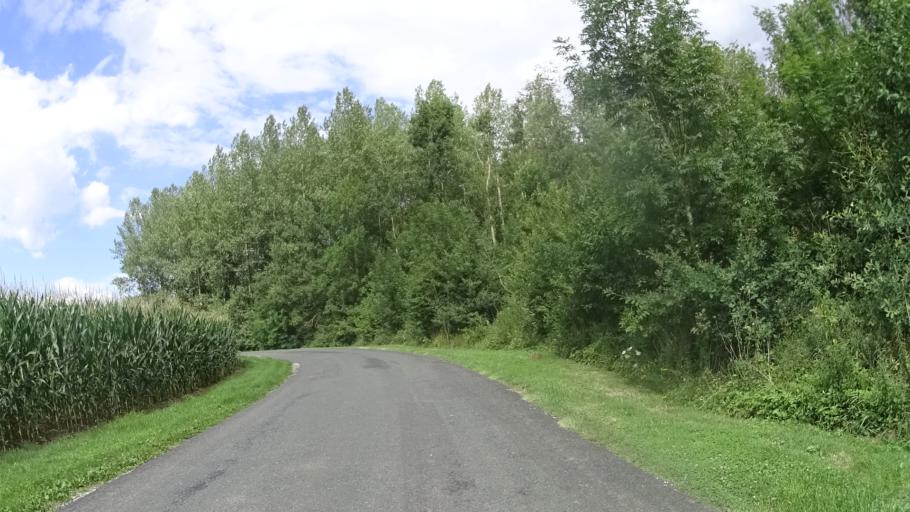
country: FR
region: Champagne-Ardenne
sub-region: Departement de la Haute-Marne
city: Villiers-en-Lieu
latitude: 48.6797
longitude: 4.8111
